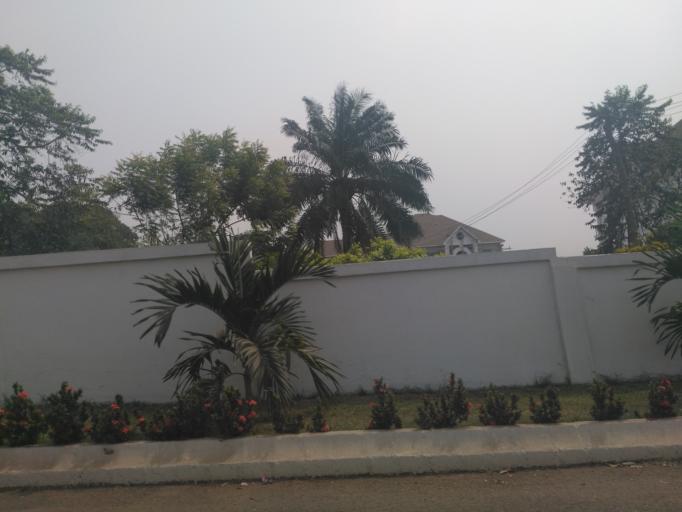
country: GH
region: Ashanti
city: Kumasi
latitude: 6.6833
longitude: -1.6321
